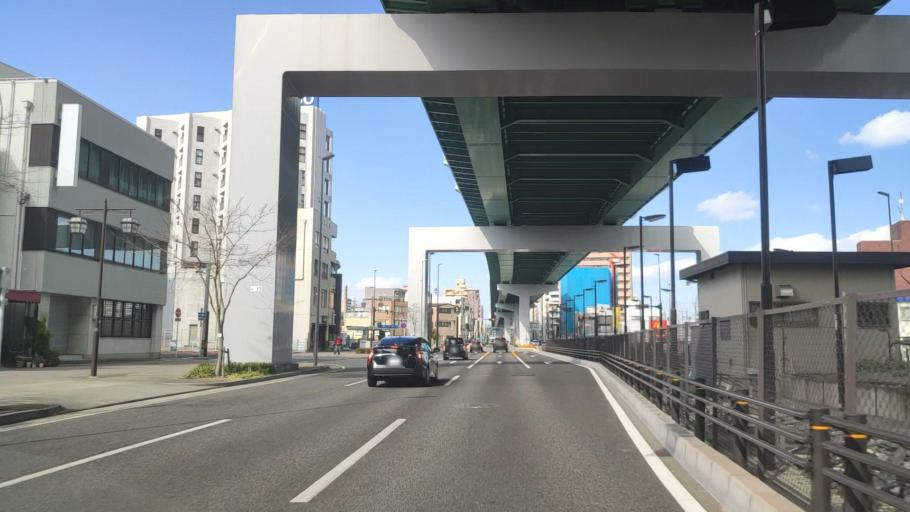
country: JP
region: Aichi
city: Nagoya-shi
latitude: 35.1824
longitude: 136.8901
